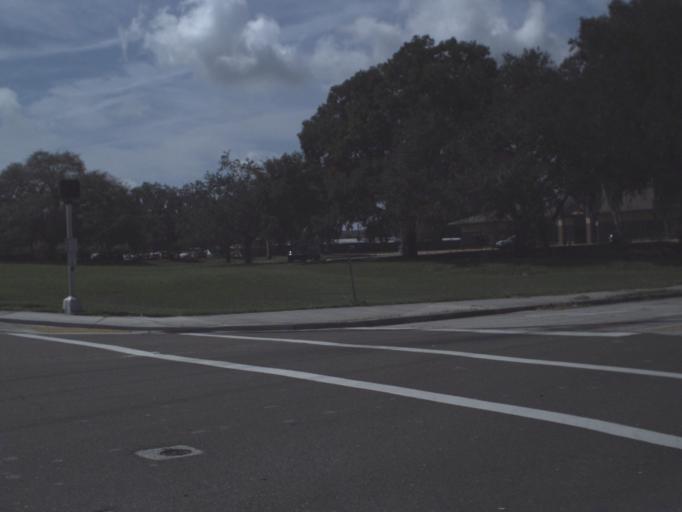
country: US
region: Florida
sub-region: Polk County
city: Winter Haven
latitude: 28.0369
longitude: -81.7269
